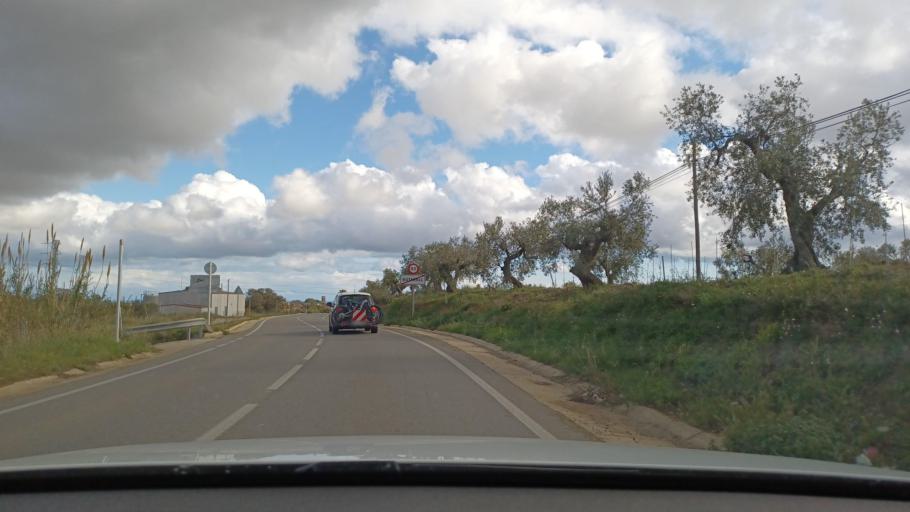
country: ES
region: Catalonia
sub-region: Provincia de Tarragona
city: Botarell
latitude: 41.1296
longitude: 0.9953
